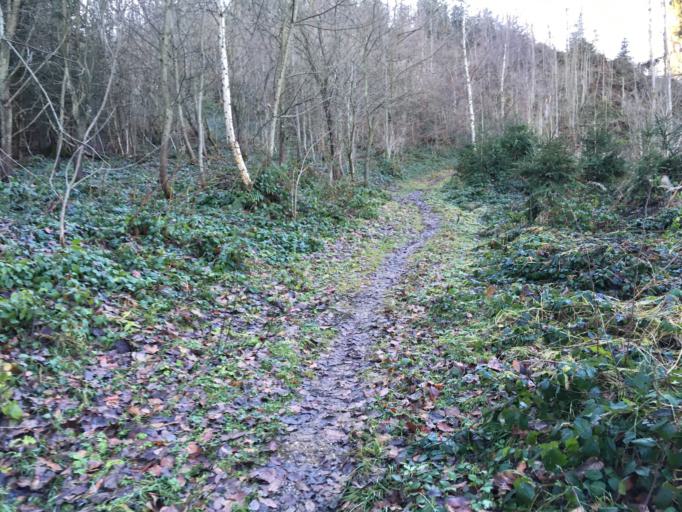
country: DE
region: Bavaria
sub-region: Swabia
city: Bohen
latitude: 47.8661
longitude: 10.2905
